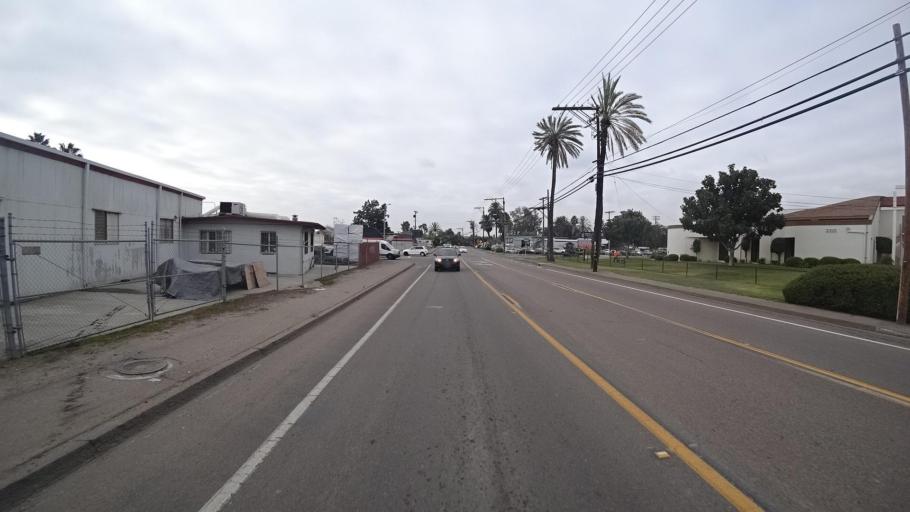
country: US
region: California
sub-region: San Diego County
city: Spring Valley
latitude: 32.7424
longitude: -117.0046
